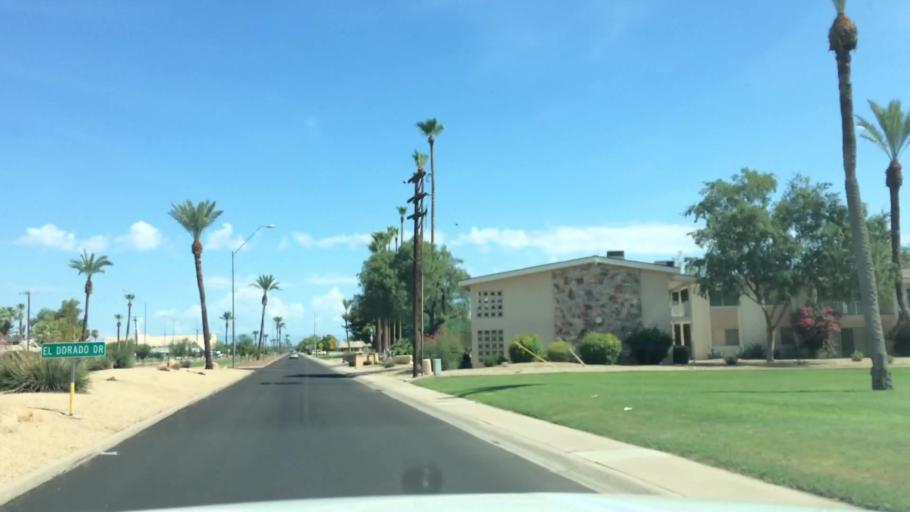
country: US
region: Arizona
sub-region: Maricopa County
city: Youngtown
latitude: 33.5822
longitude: -112.2899
